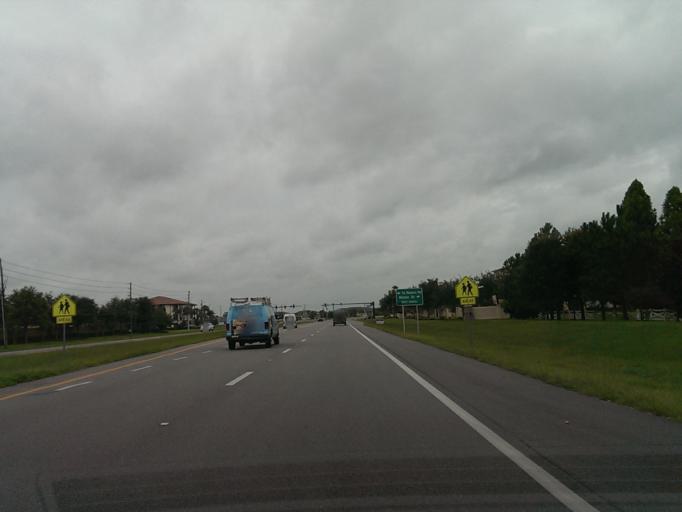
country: US
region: Florida
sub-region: Orange County
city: Bay Hill
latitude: 28.4456
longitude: -81.5552
